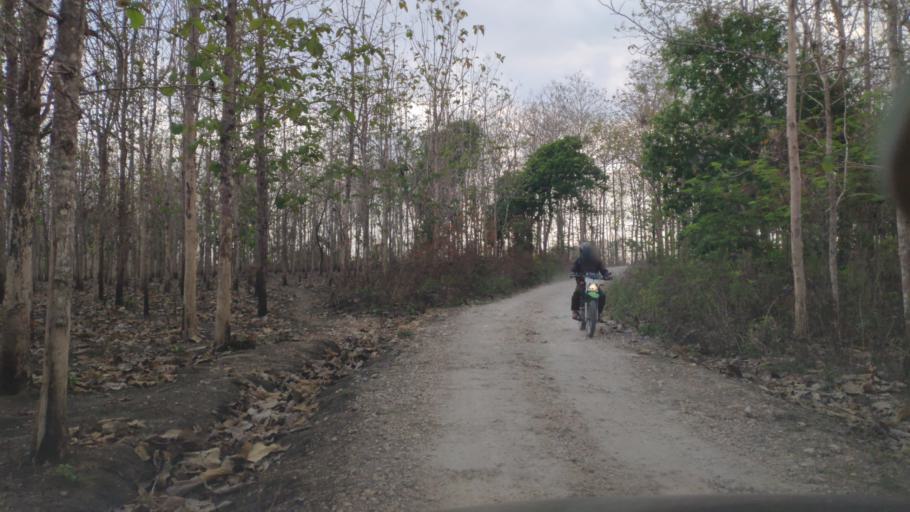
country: ID
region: Central Java
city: Randublatung
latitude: -7.2885
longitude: 111.2982
